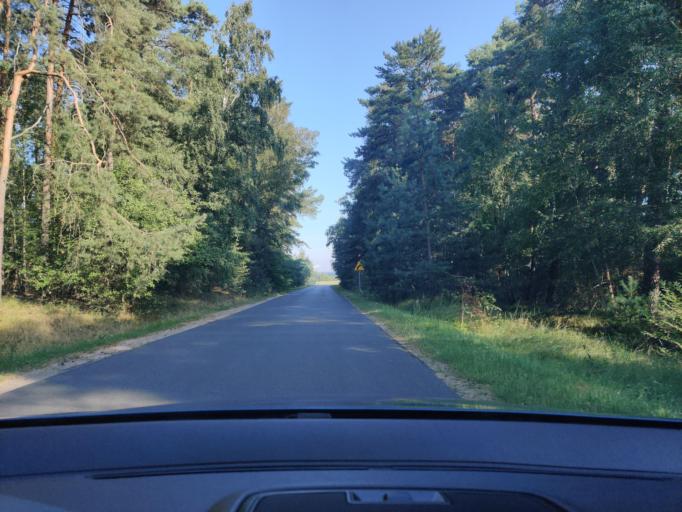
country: PL
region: Greater Poland Voivodeship
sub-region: Konin
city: Konin
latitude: 52.1824
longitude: 18.3326
